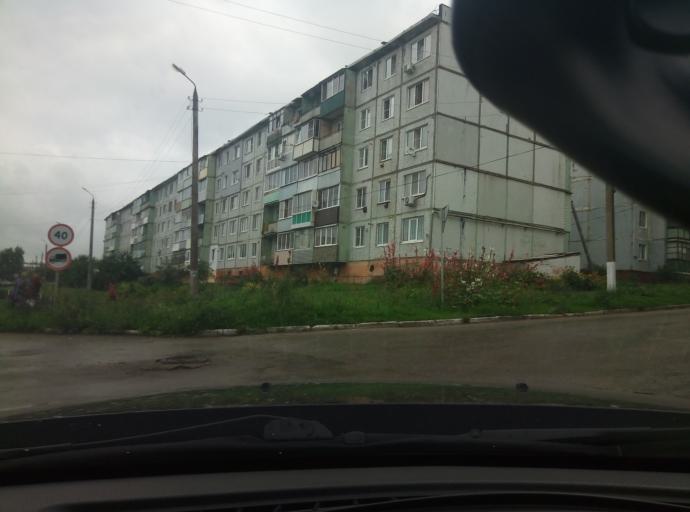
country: RU
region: Tula
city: Bolokhovo
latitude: 54.0831
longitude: 37.8234
